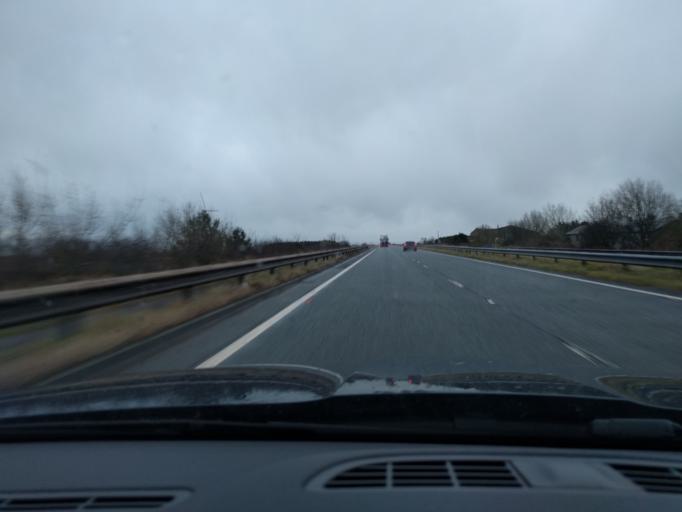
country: GB
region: England
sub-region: Northumberland
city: Berwick-Upon-Tweed
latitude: 55.7961
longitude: -2.0307
